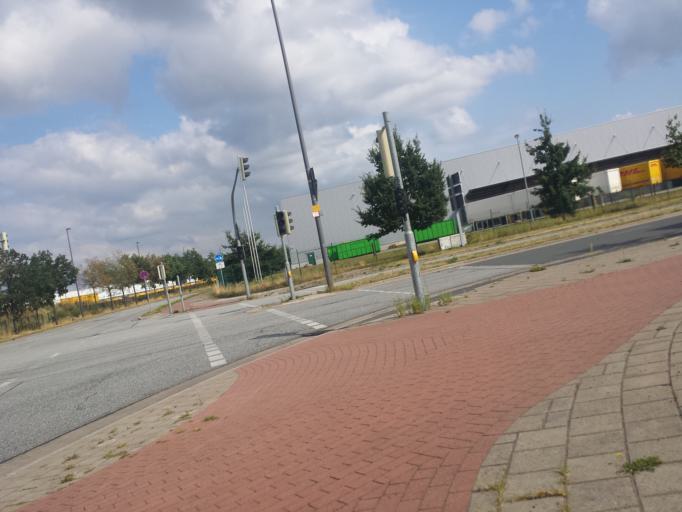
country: DE
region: Lower Saxony
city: Stuhr
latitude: 53.0985
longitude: 8.7029
